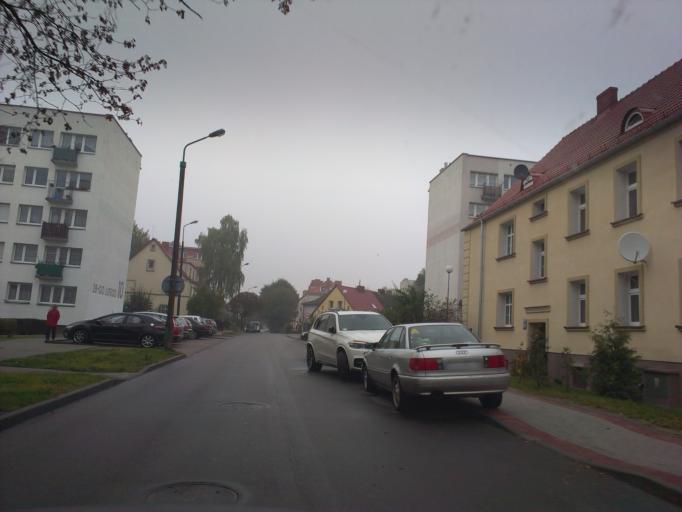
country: PL
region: West Pomeranian Voivodeship
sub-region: Powiat szczecinecki
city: Szczecinek
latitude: 53.7012
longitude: 16.7019
